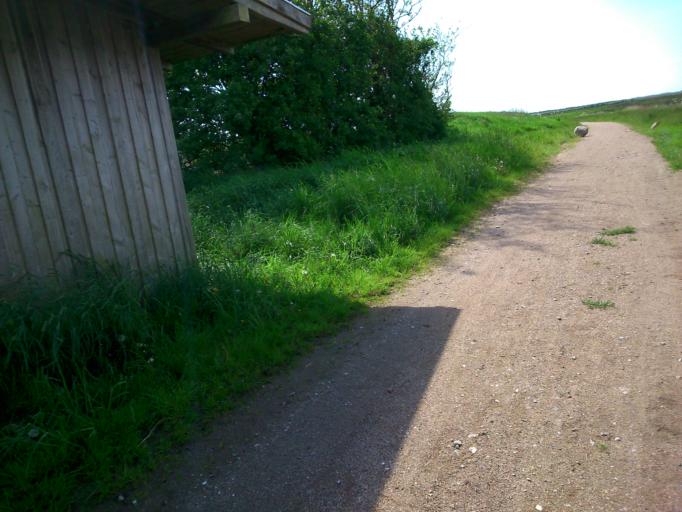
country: DK
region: Central Jutland
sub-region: Ringkobing-Skjern Kommune
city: Skjern
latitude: 55.9070
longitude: 8.4365
